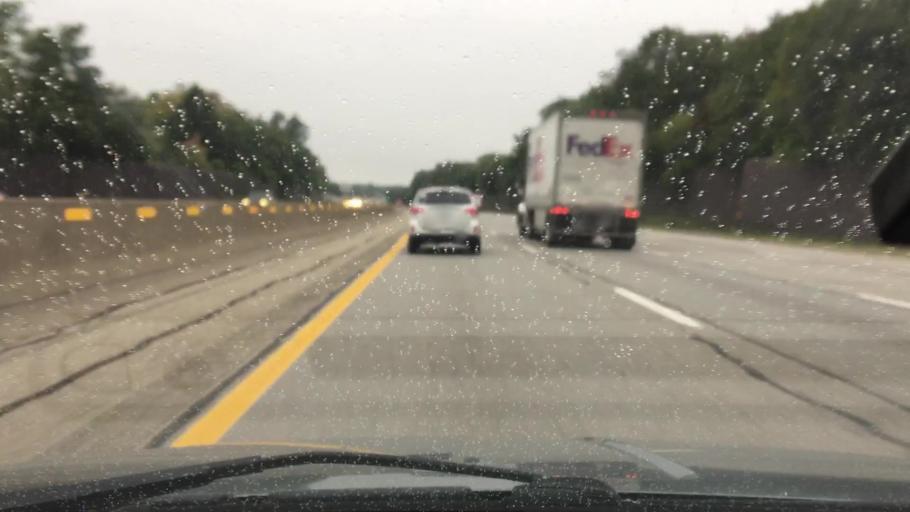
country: US
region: Michigan
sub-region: Kalamazoo County
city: Portage
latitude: 42.2444
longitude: -85.5622
